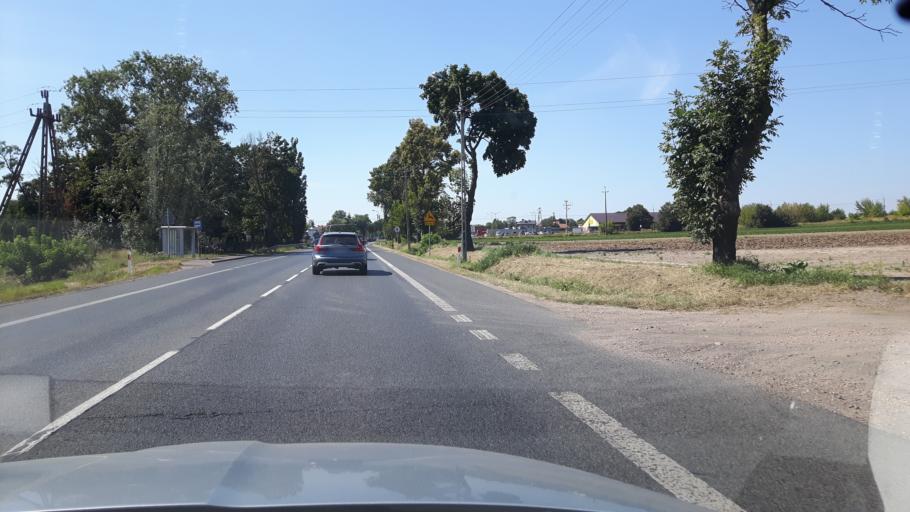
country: PL
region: Masovian Voivodeship
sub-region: Powiat nowodworski
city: Zakroczym
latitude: 52.4380
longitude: 20.6157
